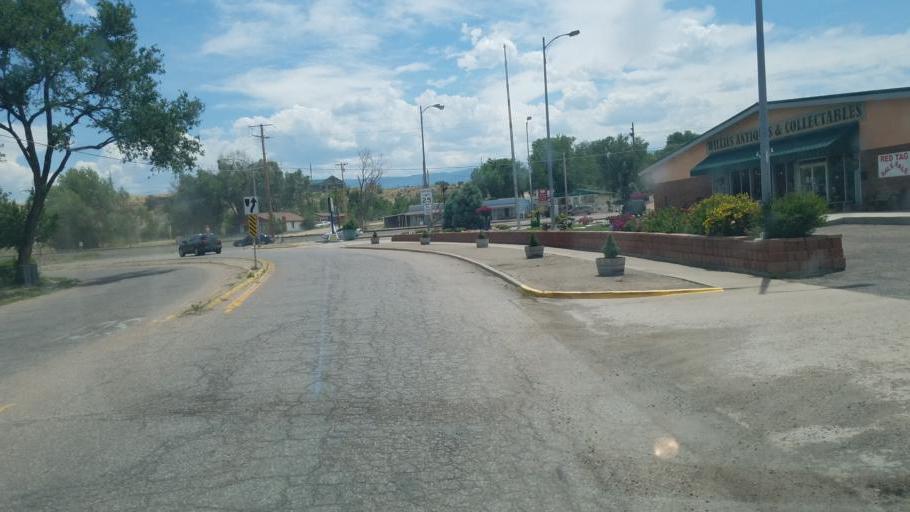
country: US
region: Colorado
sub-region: Fremont County
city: Florence
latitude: 38.3915
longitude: -105.1225
